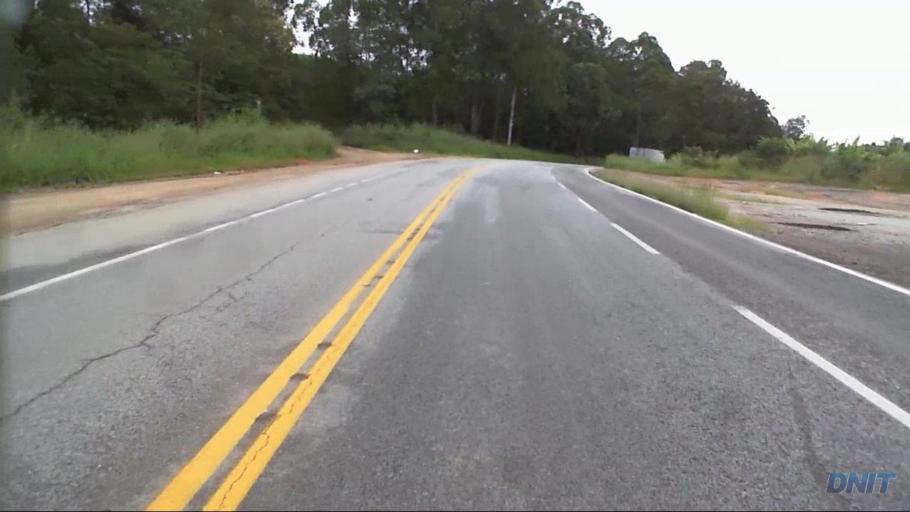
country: BR
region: Minas Gerais
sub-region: Joao Monlevade
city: Joao Monlevade
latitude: -19.8508
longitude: -43.2839
